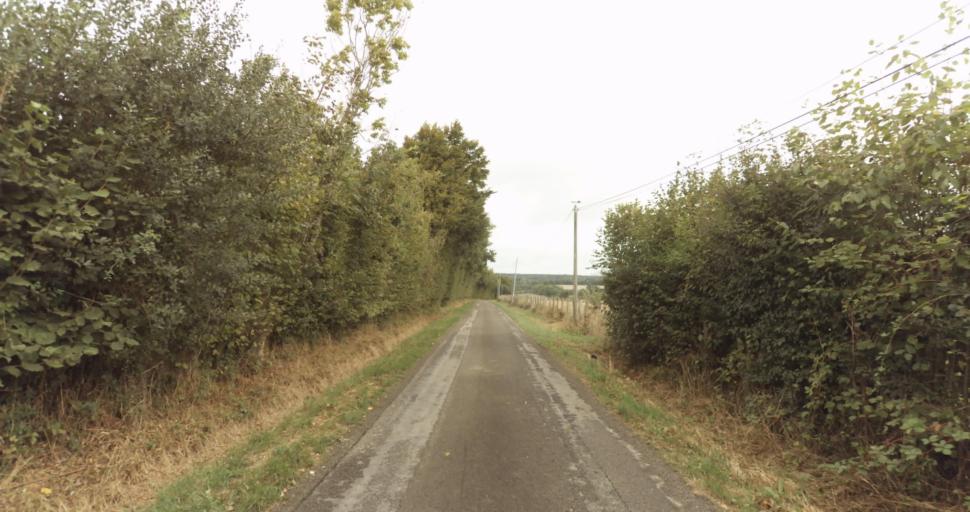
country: FR
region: Lower Normandy
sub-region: Departement de l'Orne
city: Sainte-Gauburge-Sainte-Colombe
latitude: 48.7249
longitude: 0.4785
